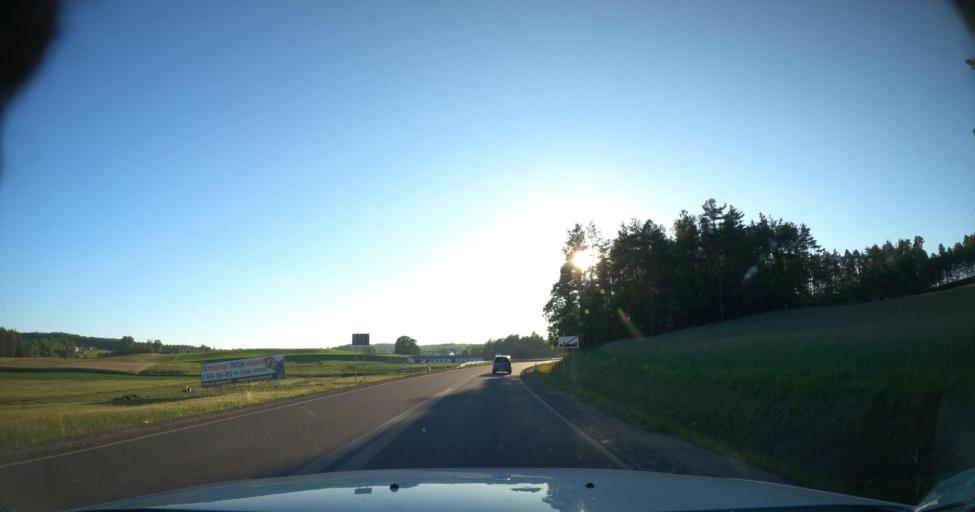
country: PL
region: Pomeranian Voivodeship
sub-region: Powiat kartuski
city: Chmielno
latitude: 54.3428
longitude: 18.0102
